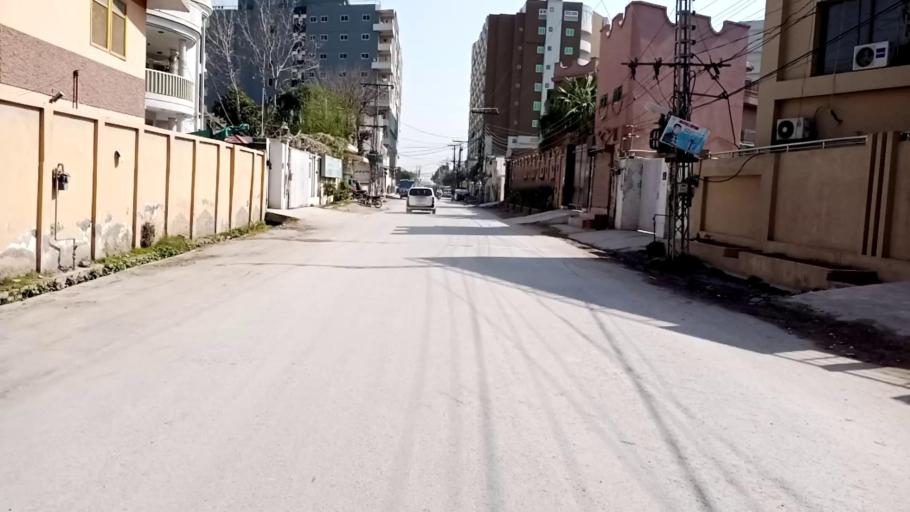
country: PK
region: Khyber Pakhtunkhwa
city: Peshawar
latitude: 33.9951
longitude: 71.5046
